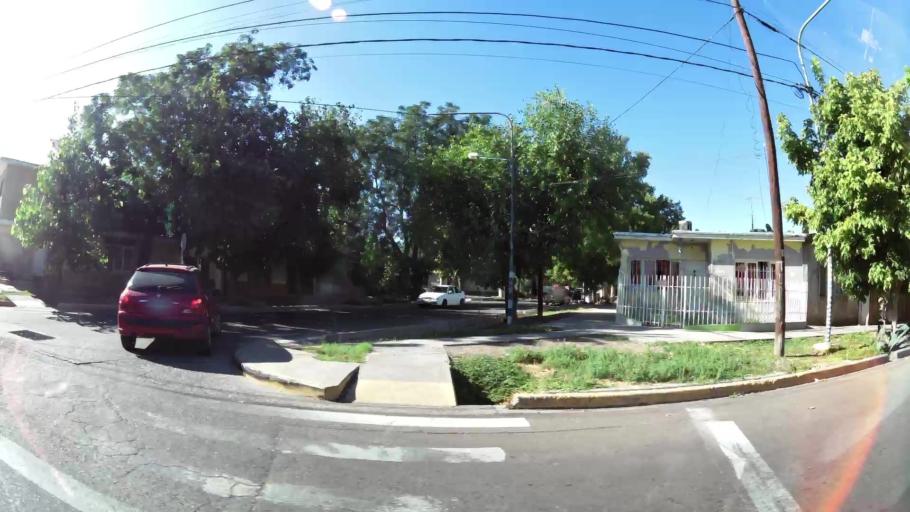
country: AR
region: Mendoza
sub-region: Departamento de Godoy Cruz
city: Godoy Cruz
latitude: -32.9230
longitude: -68.8608
